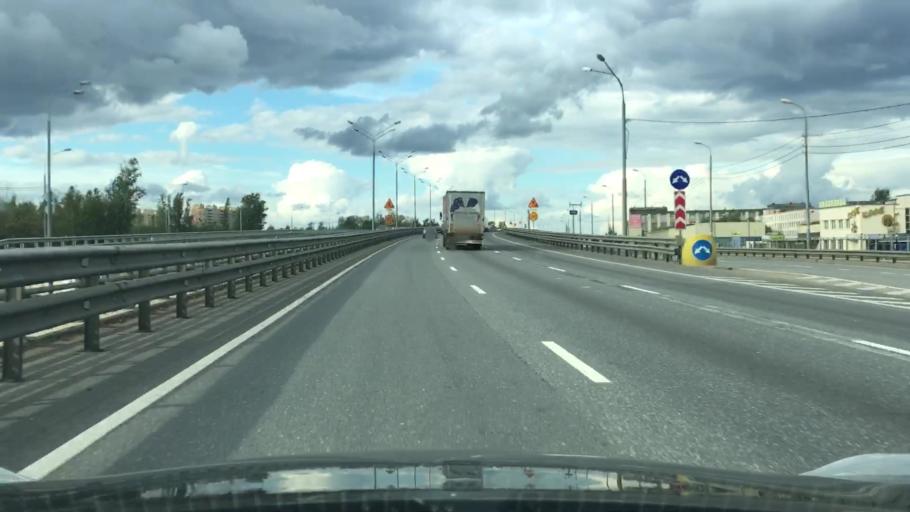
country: RU
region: Tverskaya
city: Tver
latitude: 56.8393
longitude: 35.7939
